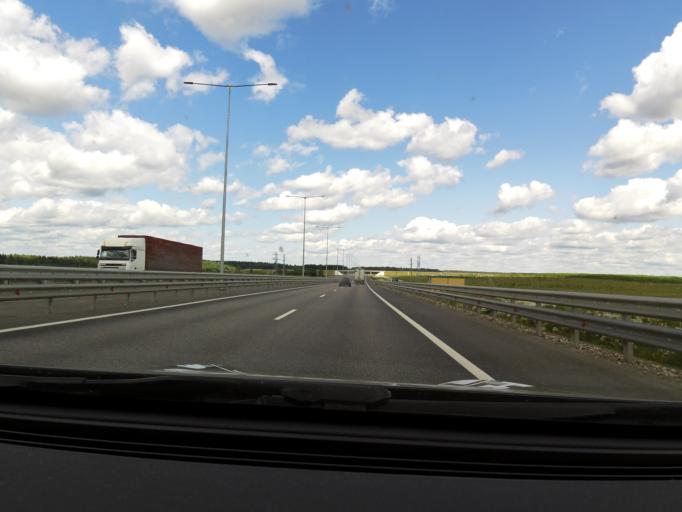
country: RU
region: Tverskaya
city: Vydropuzhsk
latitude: 57.2478
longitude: 34.8889
